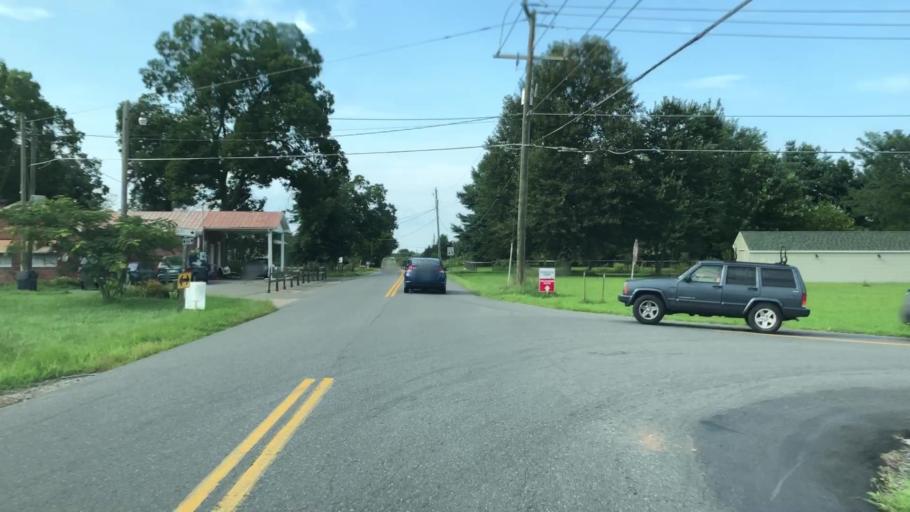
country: US
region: Virginia
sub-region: Stafford County
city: Falmouth
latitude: 38.3998
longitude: -77.5347
